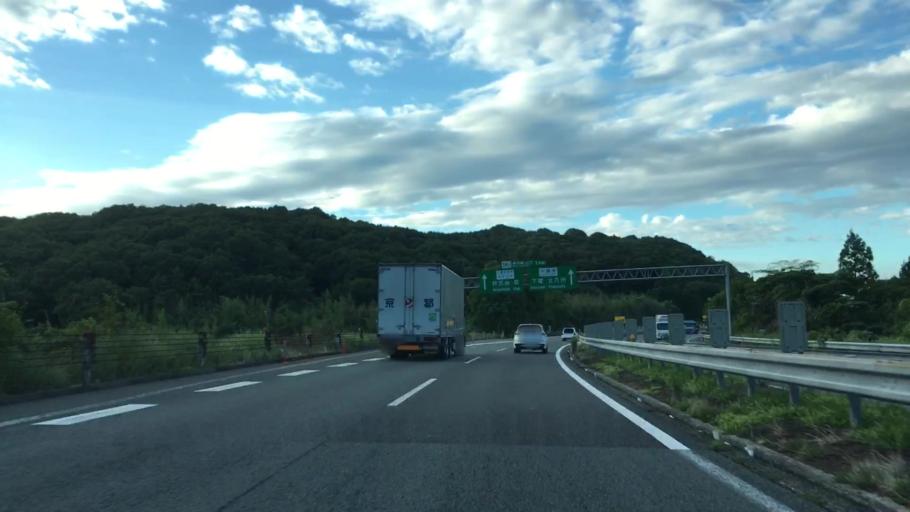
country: JP
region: Yamaguchi
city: Ogori-shimogo
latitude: 34.1640
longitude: 131.3264
